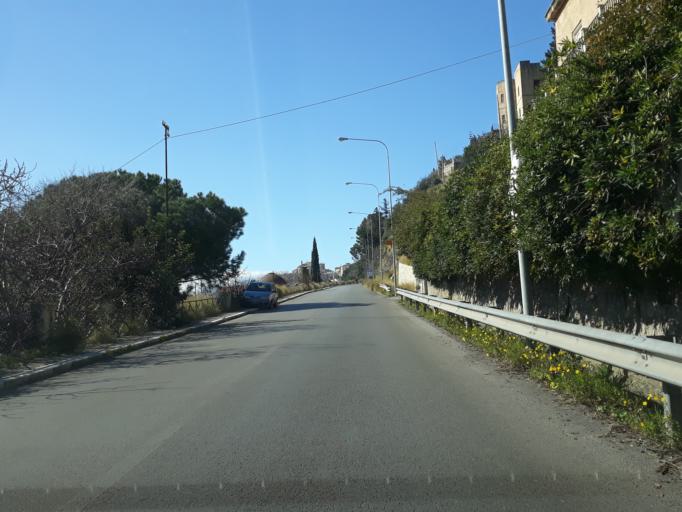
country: IT
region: Sicily
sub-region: Palermo
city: Monreale
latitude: 38.0898
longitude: 13.3007
